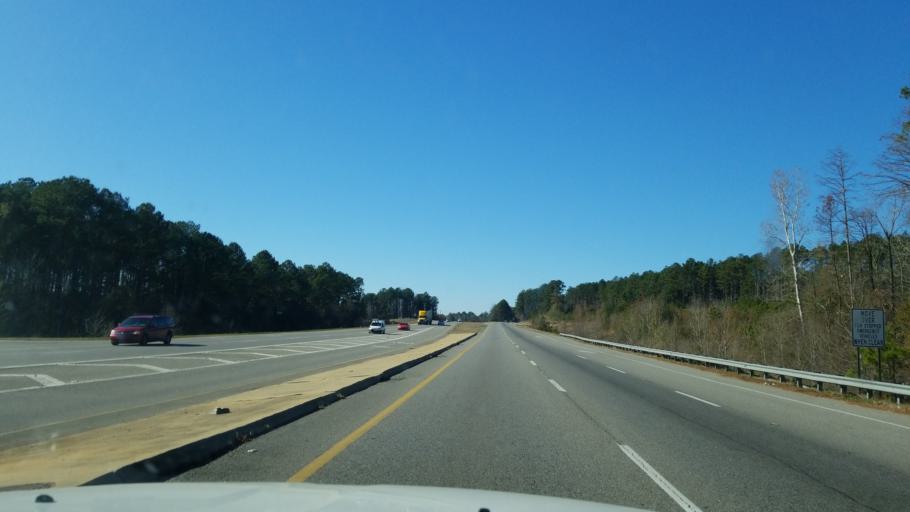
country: US
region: Alabama
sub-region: Tuscaloosa County
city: Northport
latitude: 33.2345
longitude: -87.6397
